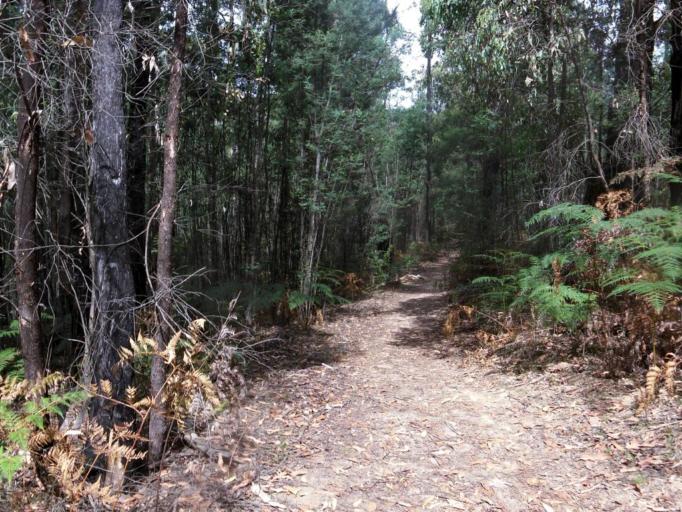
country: AU
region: Victoria
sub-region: Yarra Ranges
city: Healesville
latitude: -37.4029
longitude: 145.5654
